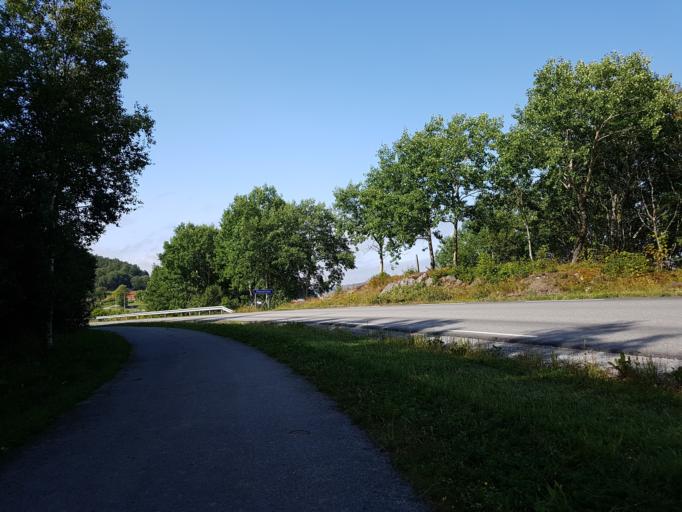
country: NO
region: Sor-Trondelag
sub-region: Agdenes
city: Lensvik
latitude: 63.6348
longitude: 9.8328
